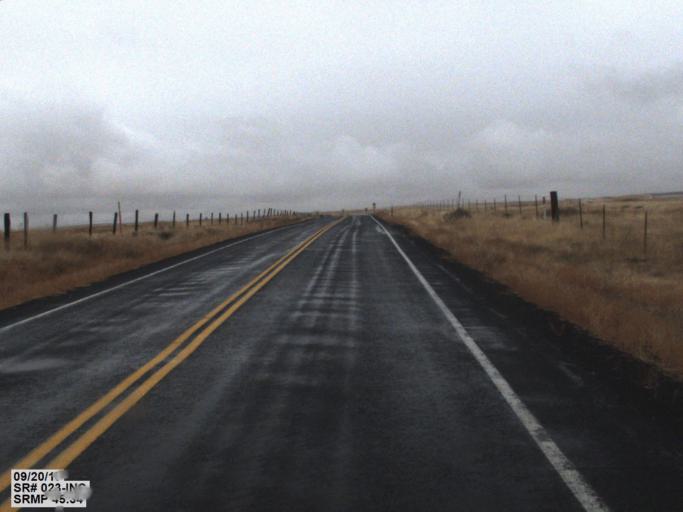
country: US
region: Washington
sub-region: Lincoln County
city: Davenport
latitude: 47.3296
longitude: -117.9833
